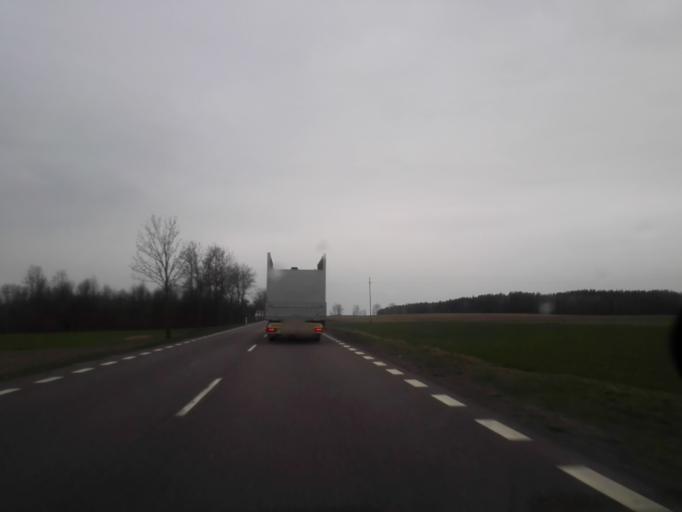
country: PL
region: Podlasie
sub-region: Powiat grajewski
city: Grajewo
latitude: 53.6081
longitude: 22.3730
